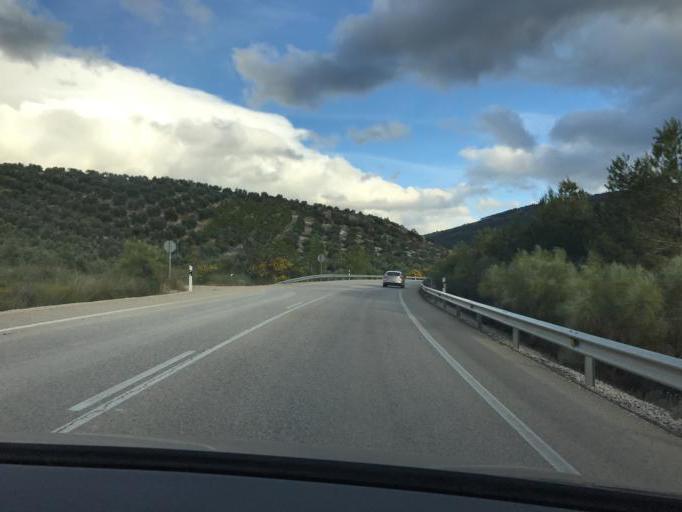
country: ES
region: Andalusia
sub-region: Provincia de Jaen
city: Jodar
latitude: 37.8041
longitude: -3.3639
